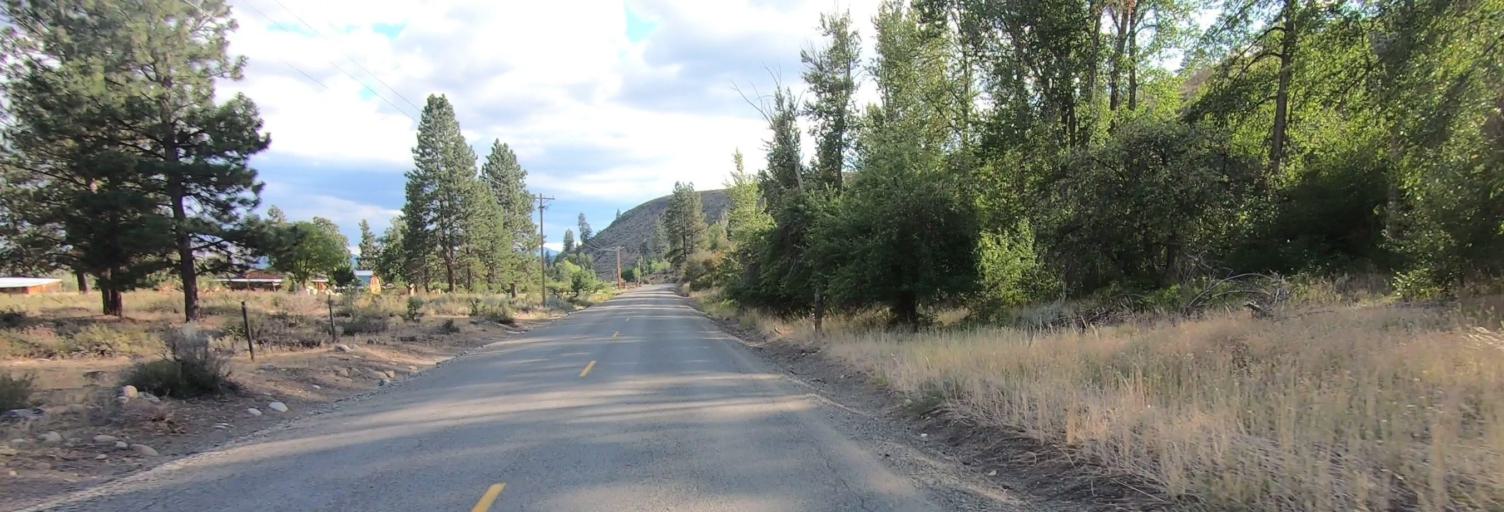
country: US
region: Washington
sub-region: Okanogan County
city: Brewster
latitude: 48.5314
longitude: -120.1909
